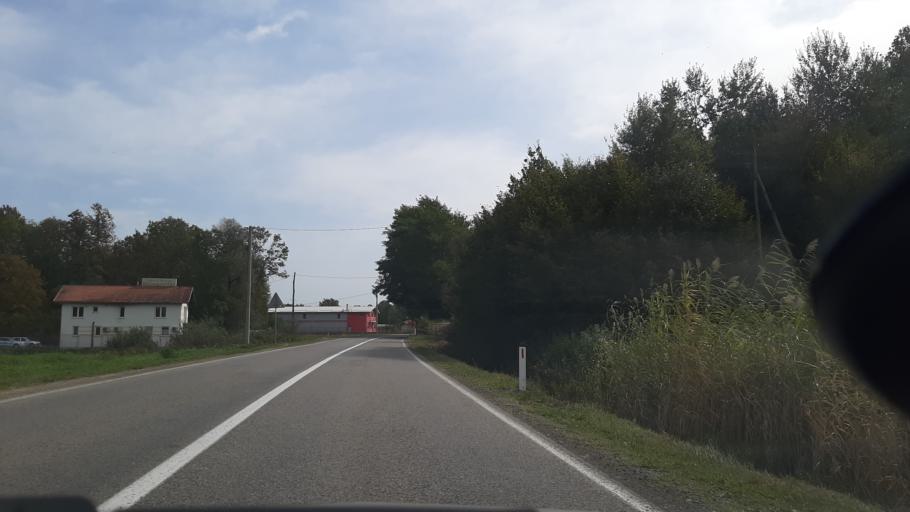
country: BA
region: Republika Srpska
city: Maglajani
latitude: 44.8791
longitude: 17.3760
